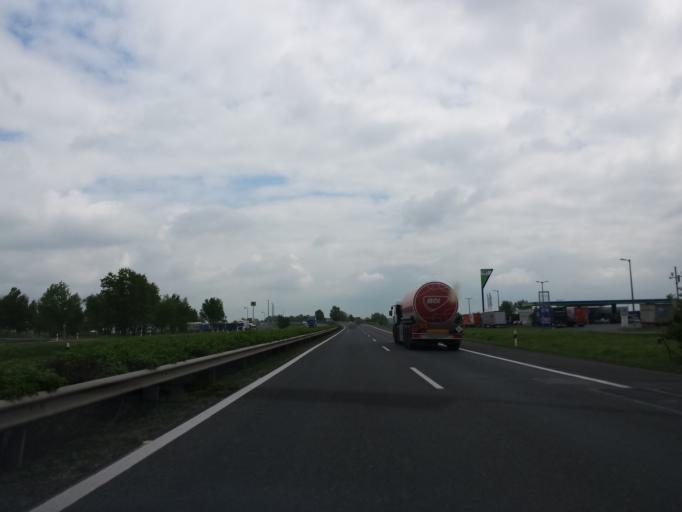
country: HU
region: Gyor-Moson-Sopron
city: Gyorujbarat
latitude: 47.6352
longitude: 17.6612
